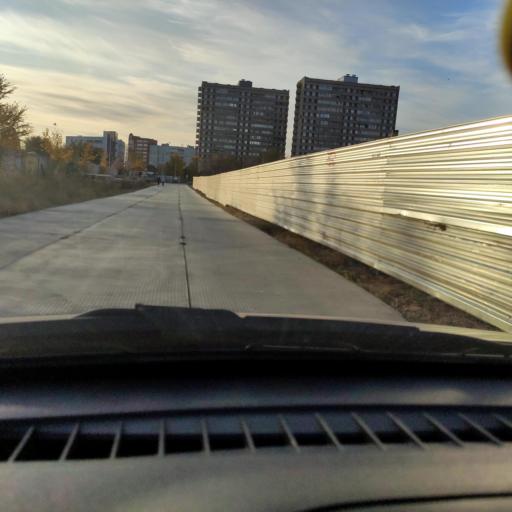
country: RU
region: Samara
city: Tol'yatti
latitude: 53.5257
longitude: 49.3324
